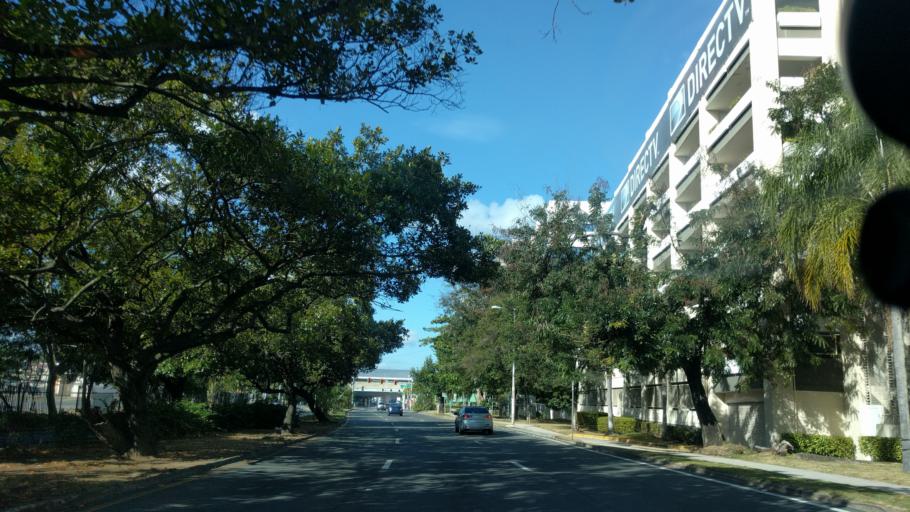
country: PR
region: Catano
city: Catano
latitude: 18.4244
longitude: -66.0559
